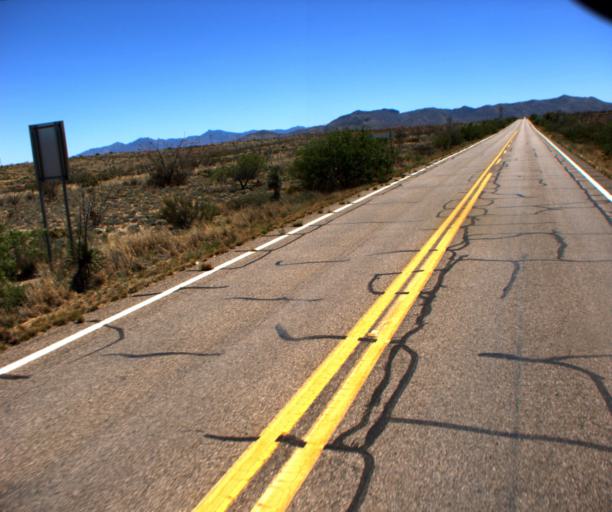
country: US
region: Arizona
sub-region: Pima County
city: Vail
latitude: 31.9976
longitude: -110.6867
